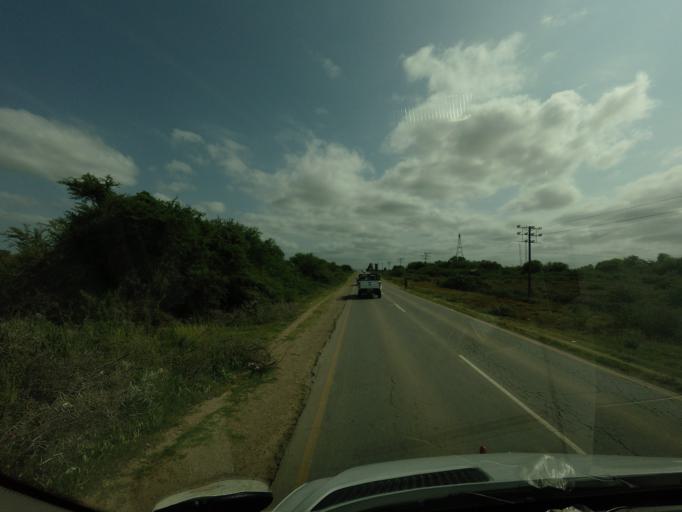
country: ZA
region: Eastern Cape
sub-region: Cacadu District Municipality
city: Kirkwood
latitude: -33.5444
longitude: 25.6899
